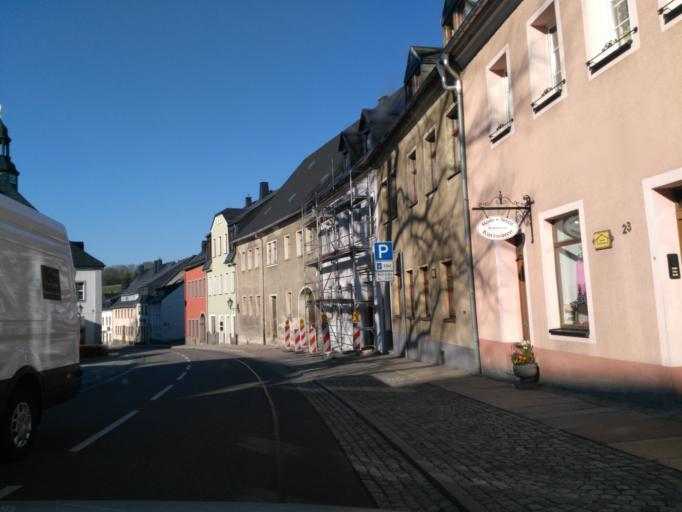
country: DE
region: Saxony
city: Schlettau
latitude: 50.5586
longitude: 12.9513
